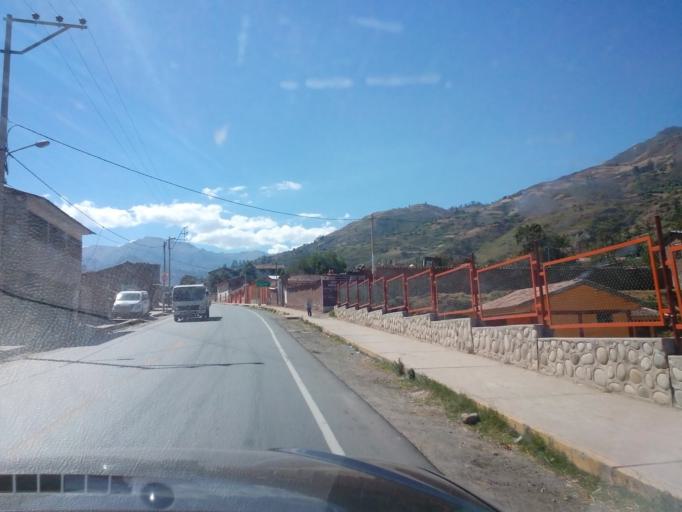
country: PE
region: Cusco
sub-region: Provincia de Anta
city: Limatambo
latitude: -13.4816
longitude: -72.4477
